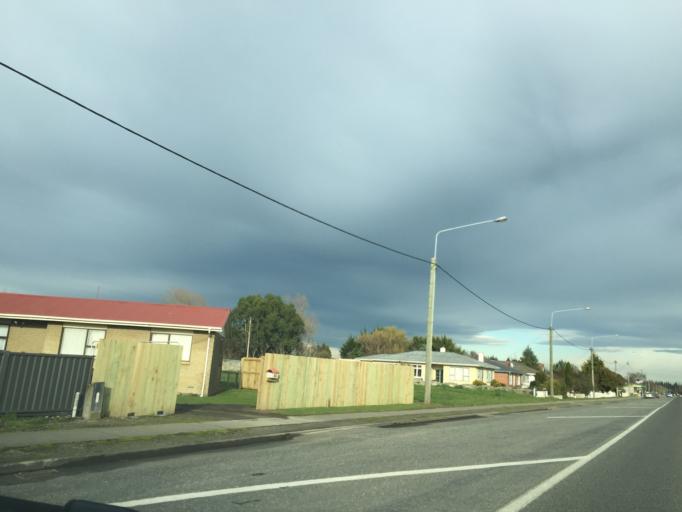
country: NZ
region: Southland
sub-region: Gore District
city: Gore
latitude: -46.1957
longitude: 168.8628
